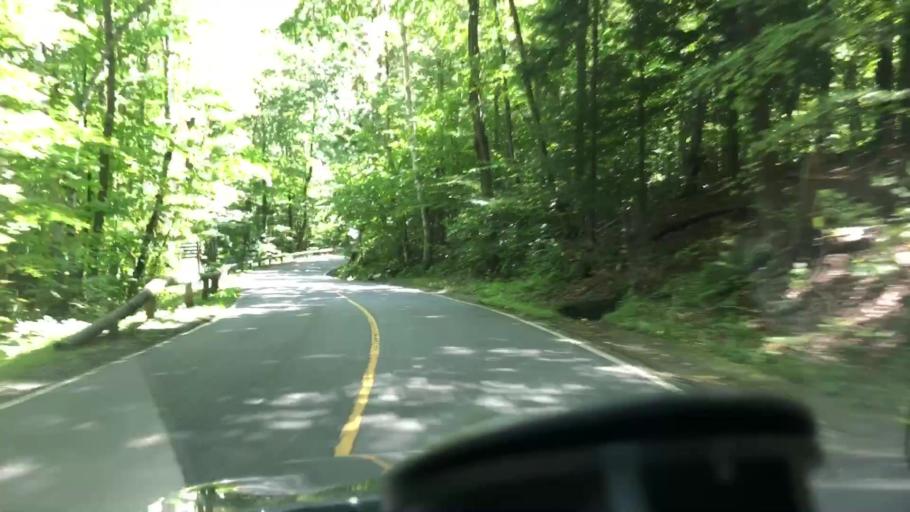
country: US
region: Massachusetts
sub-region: Berkshire County
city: North Adams
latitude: 42.6764
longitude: -73.1437
